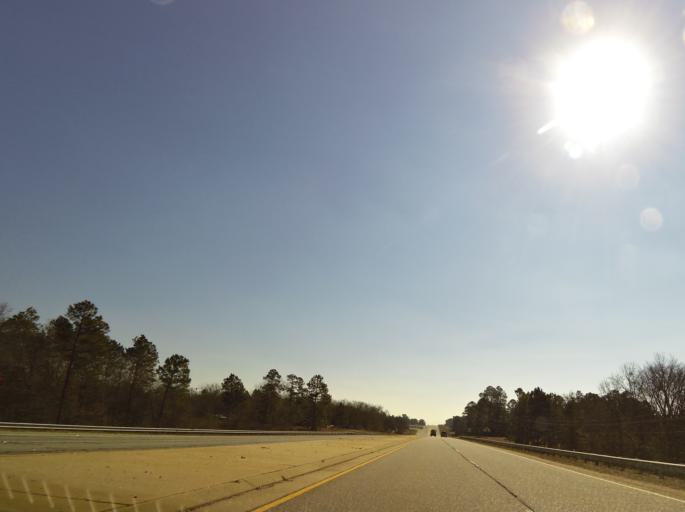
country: US
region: Georgia
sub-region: Pulaski County
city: Hawkinsville
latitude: 32.3082
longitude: -83.5062
